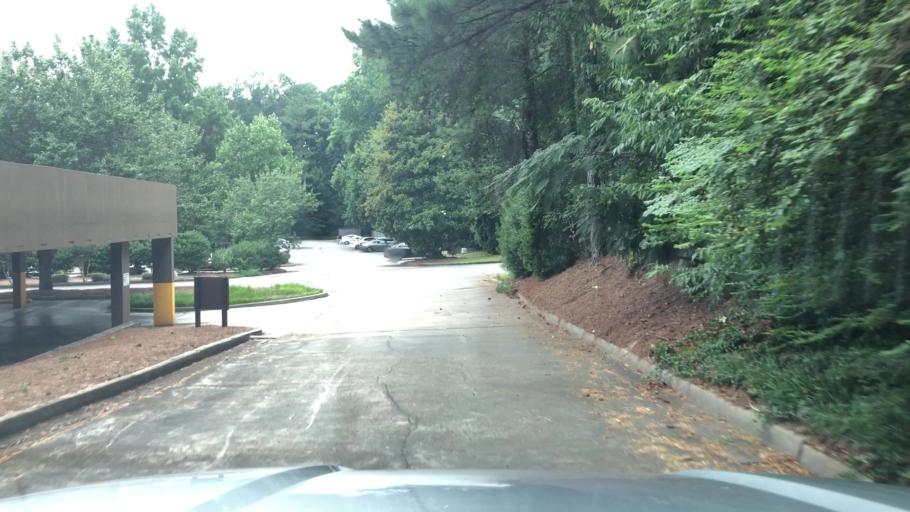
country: US
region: Georgia
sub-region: Fulton County
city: Sandy Springs
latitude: 33.9788
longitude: -84.4369
